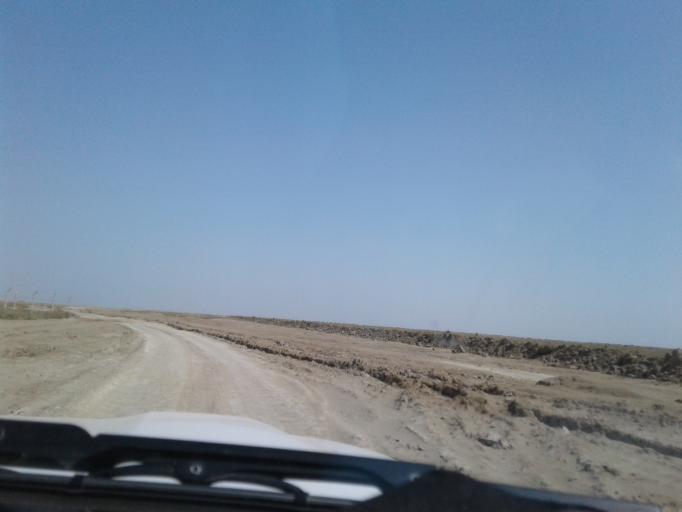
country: IR
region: Golestan
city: Gomishan
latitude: 37.8204
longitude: 53.9225
